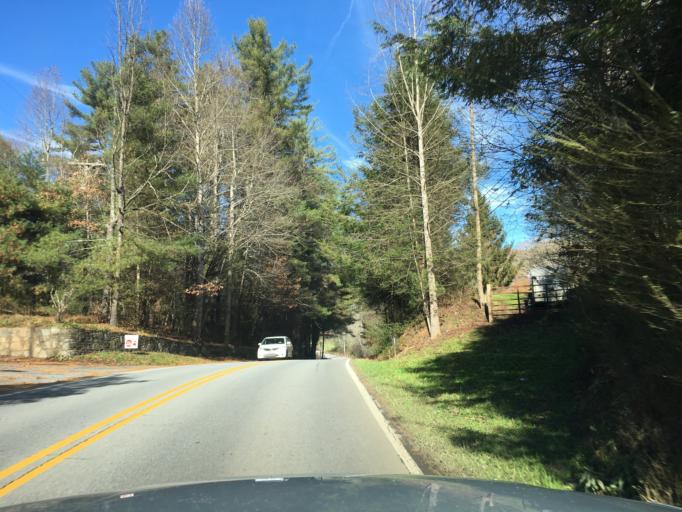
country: US
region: North Carolina
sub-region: Henderson County
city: Etowah
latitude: 35.2446
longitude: -82.6320
